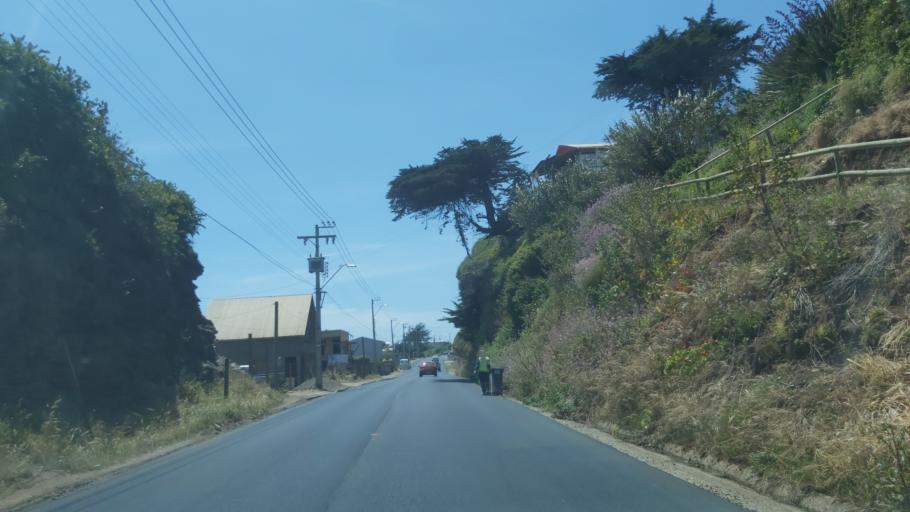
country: CL
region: Maule
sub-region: Provincia de Cauquenes
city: Cauquenes
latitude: -35.8208
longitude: -72.5982
